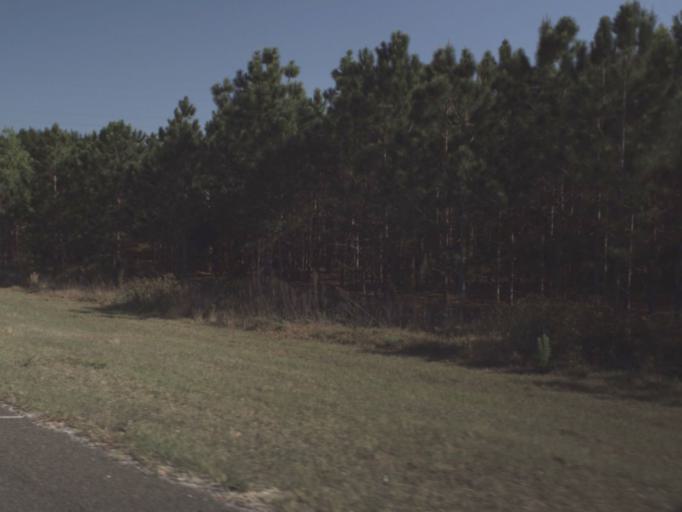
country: US
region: Florida
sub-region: Lake County
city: Minneola
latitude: 28.6065
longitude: -81.7566
